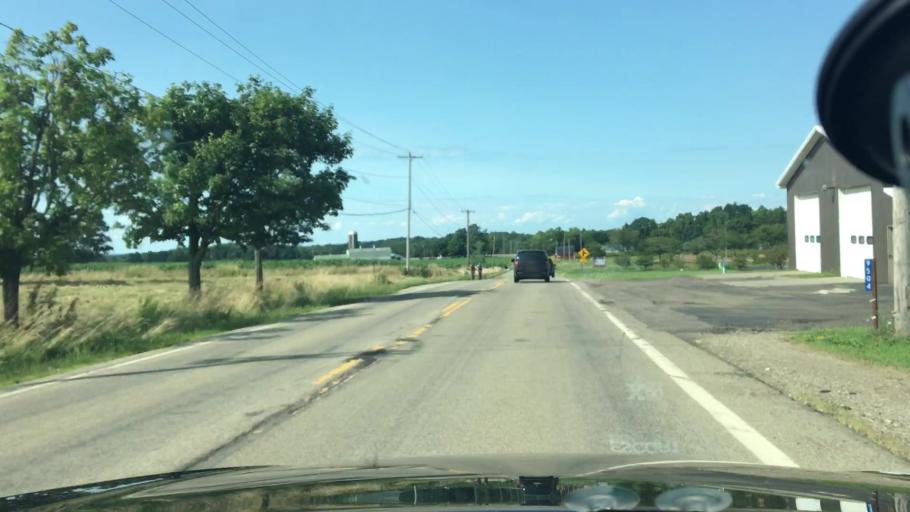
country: US
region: New York
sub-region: Chautauqua County
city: Fredonia
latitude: 42.4150
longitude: -79.3126
